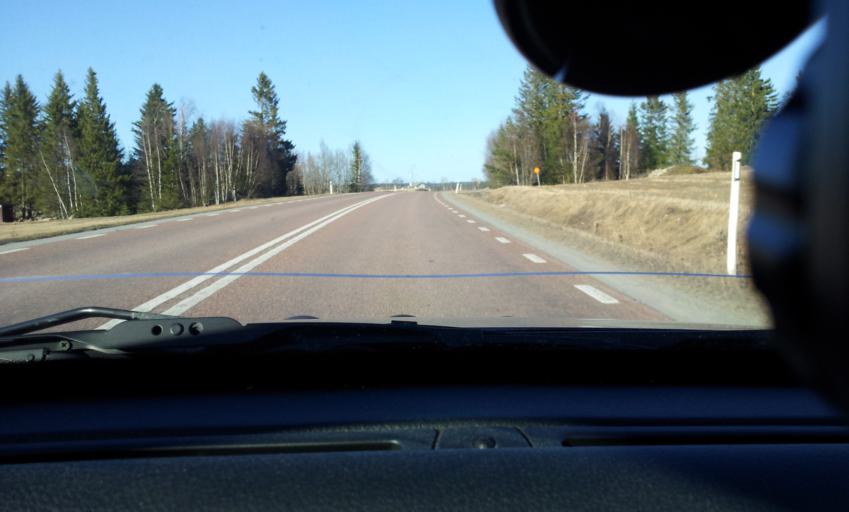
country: SE
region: Jaemtland
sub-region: OEstersunds Kommun
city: Ostersund
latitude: 62.9819
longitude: 14.5702
